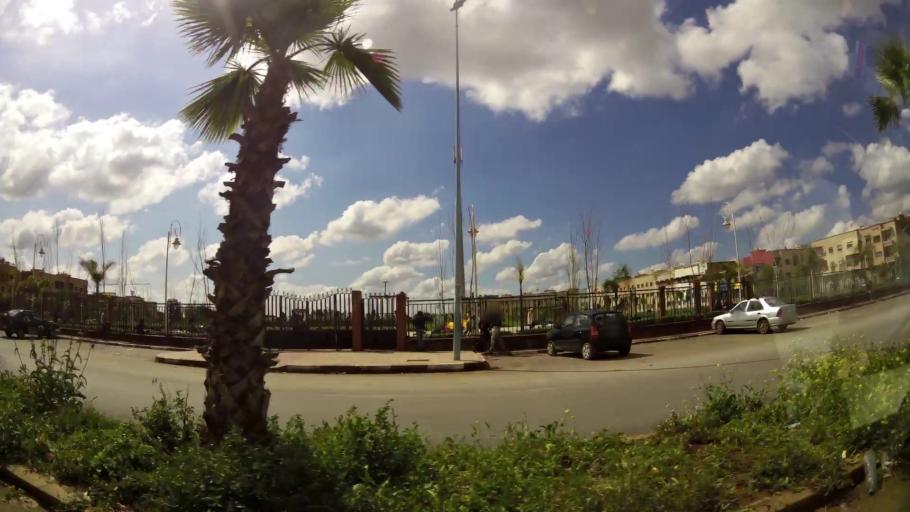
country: MA
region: Grand Casablanca
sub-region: Mediouna
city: Mediouna
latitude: 33.3774
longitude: -7.5360
